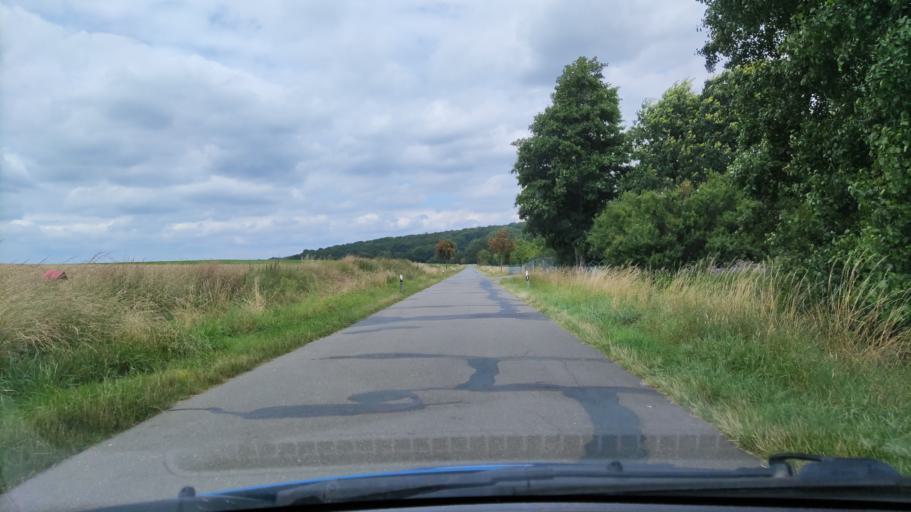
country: DE
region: Lower Saxony
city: Weste
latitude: 53.0742
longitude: 10.6895
